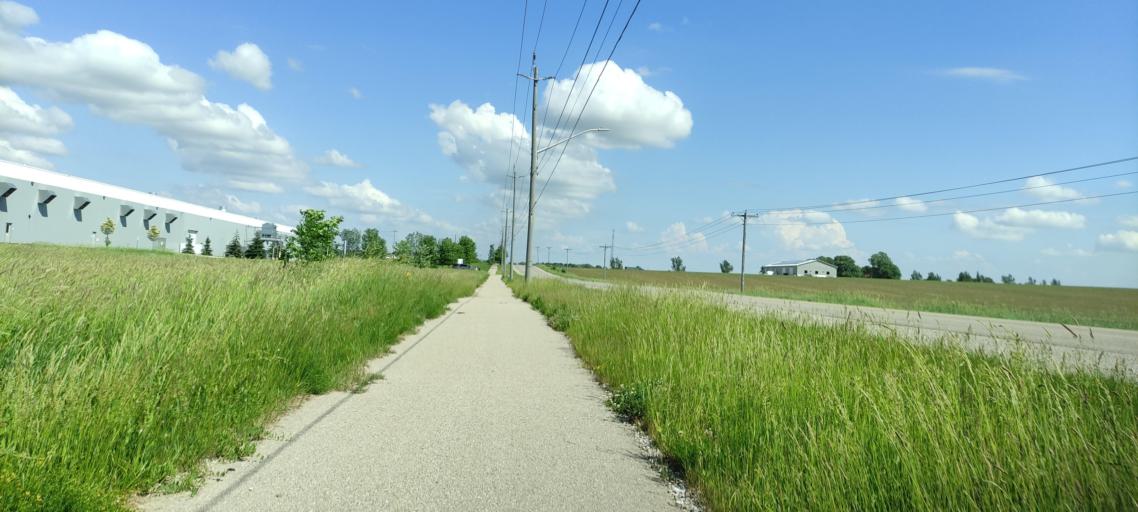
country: CA
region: Ontario
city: Stratford
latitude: 43.3437
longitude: -81.0169
